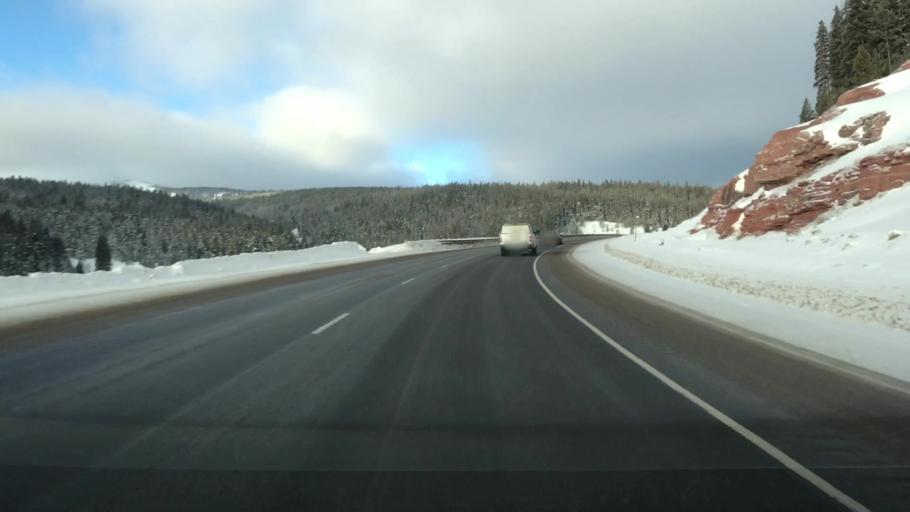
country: US
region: Colorado
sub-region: Summit County
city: Frisco
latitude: 39.5064
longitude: -106.1970
